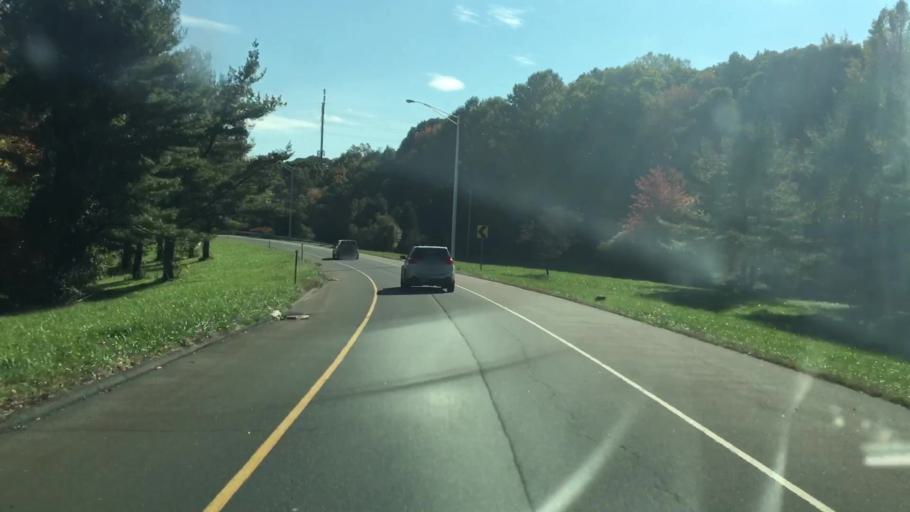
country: US
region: Connecticut
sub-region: Fairfield County
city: Trumbull
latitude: 41.2342
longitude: -73.1917
